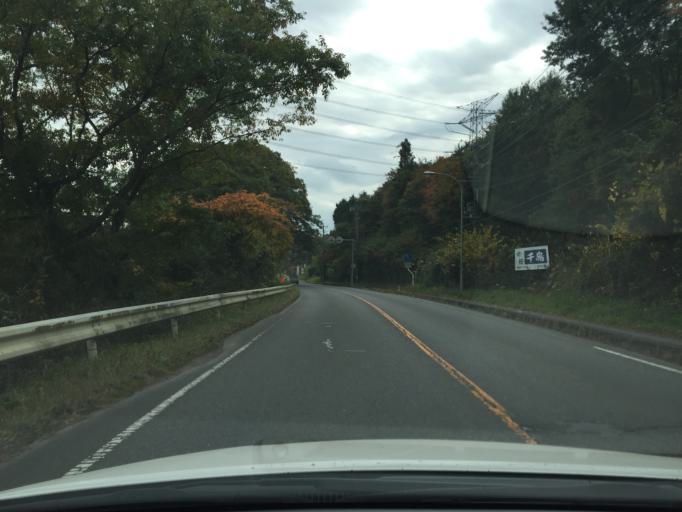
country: JP
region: Fukushima
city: Ishikawa
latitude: 37.0531
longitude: 140.3740
